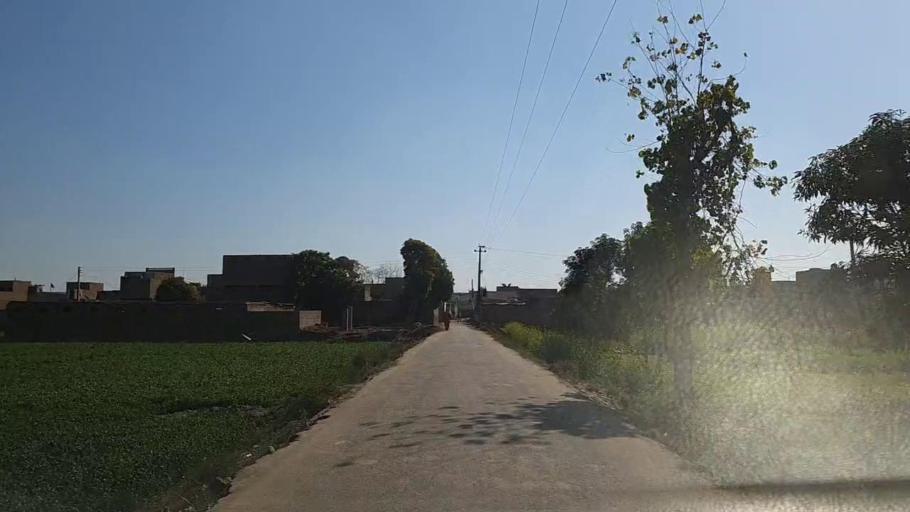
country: PK
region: Sindh
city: Nawabshah
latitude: 26.2569
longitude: 68.4242
